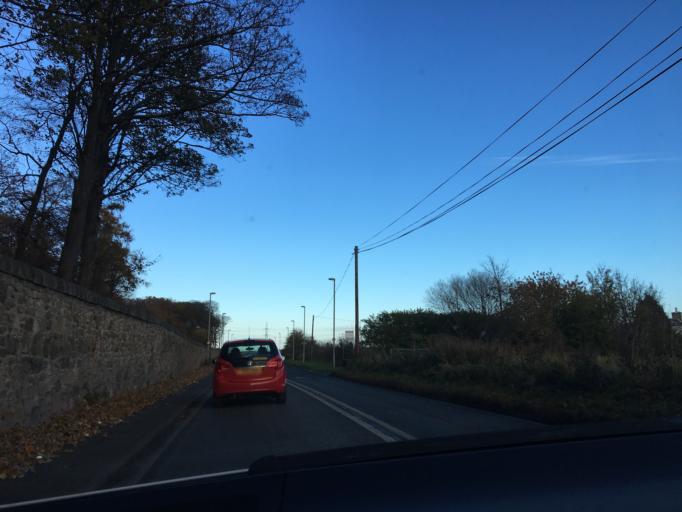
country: GB
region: Scotland
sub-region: Midlothian
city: Dalkeith
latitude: 55.9052
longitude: -3.0486
